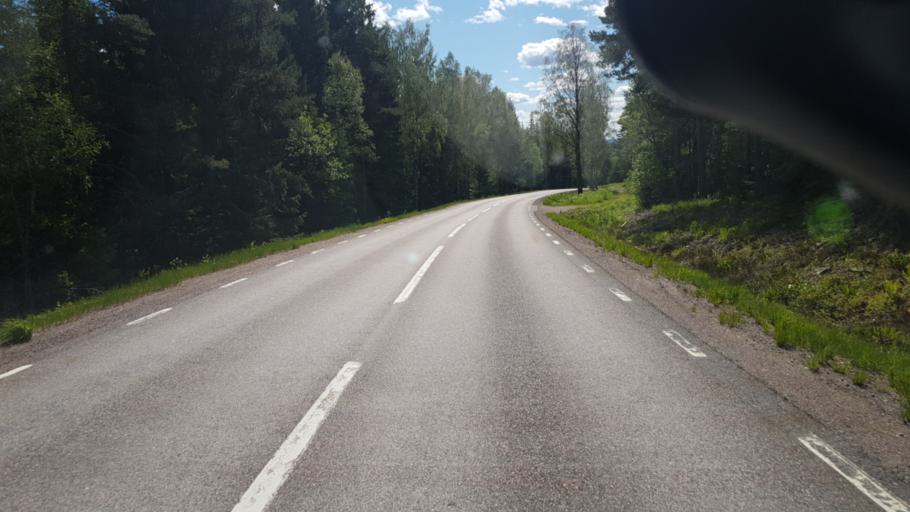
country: SE
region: Vaermland
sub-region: Sunne Kommun
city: Sunne
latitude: 59.6821
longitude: 13.0465
